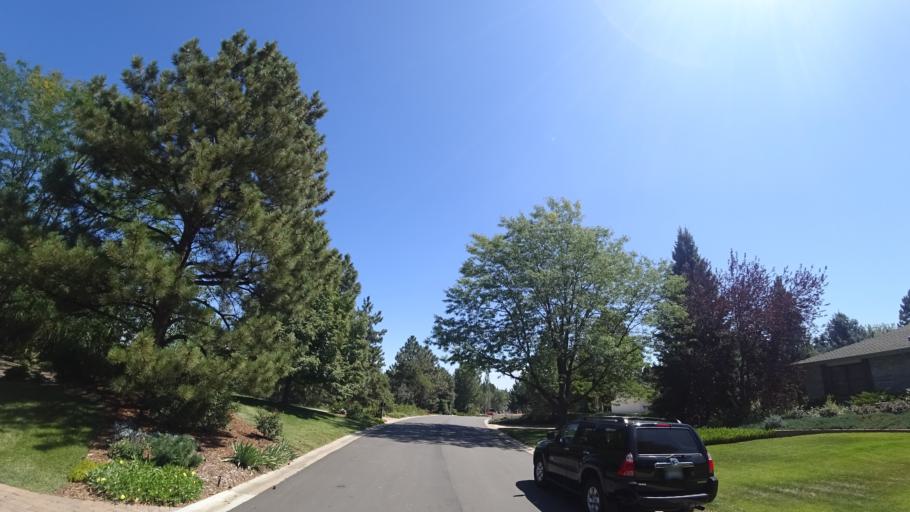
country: US
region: Colorado
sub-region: Arapahoe County
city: Greenwood Village
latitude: 39.6108
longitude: -104.9580
